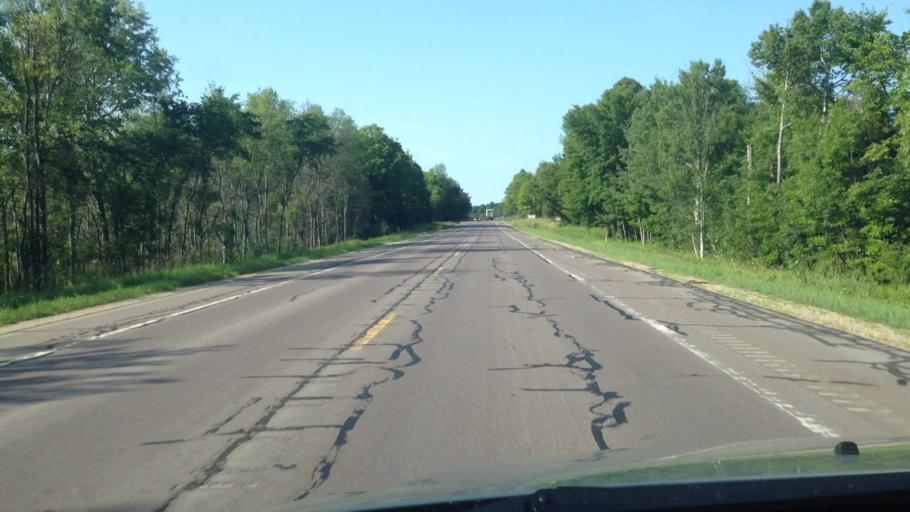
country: US
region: Michigan
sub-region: Schoolcraft County
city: Manistique
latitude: 46.0916
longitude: -85.9507
